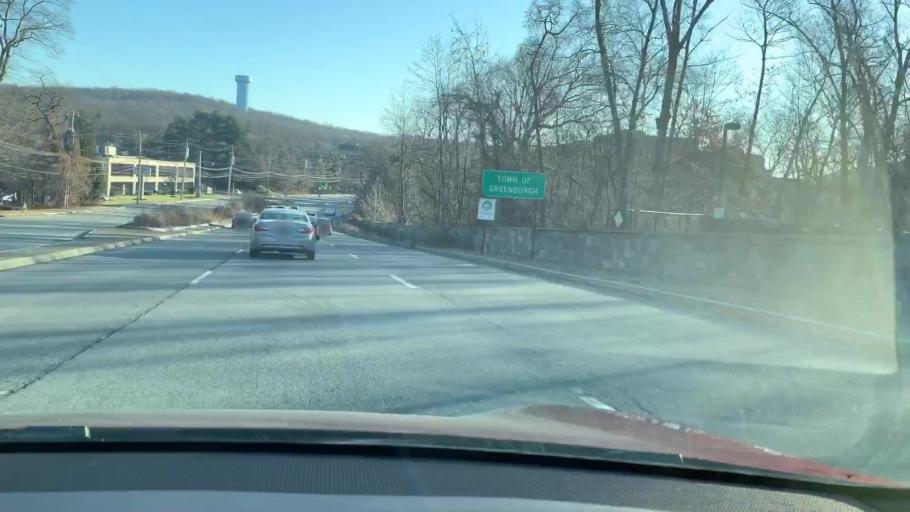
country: US
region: New York
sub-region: Westchester County
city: Tarrytown
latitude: 41.0633
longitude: -73.8435
